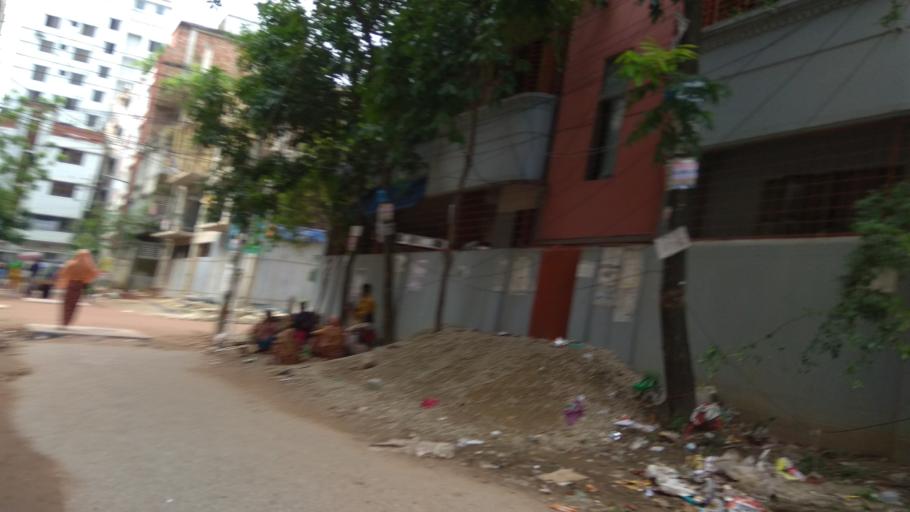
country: BD
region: Dhaka
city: Azimpur
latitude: 23.8148
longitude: 90.3543
